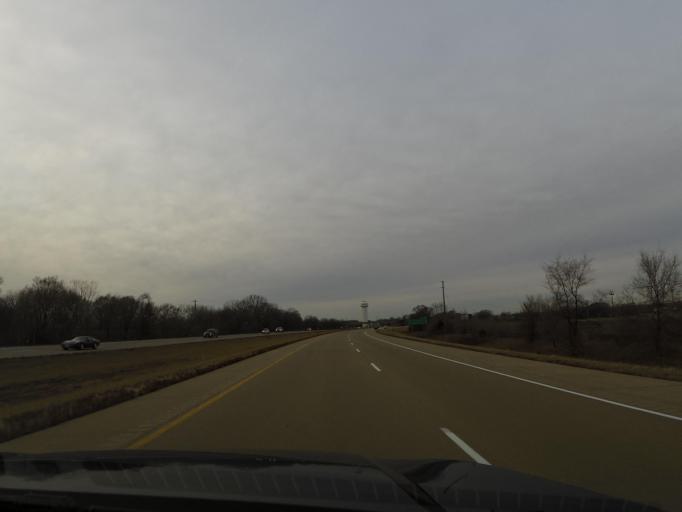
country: US
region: Iowa
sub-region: Black Hawk County
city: Elk Run Heights
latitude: 42.4532
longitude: -92.2493
